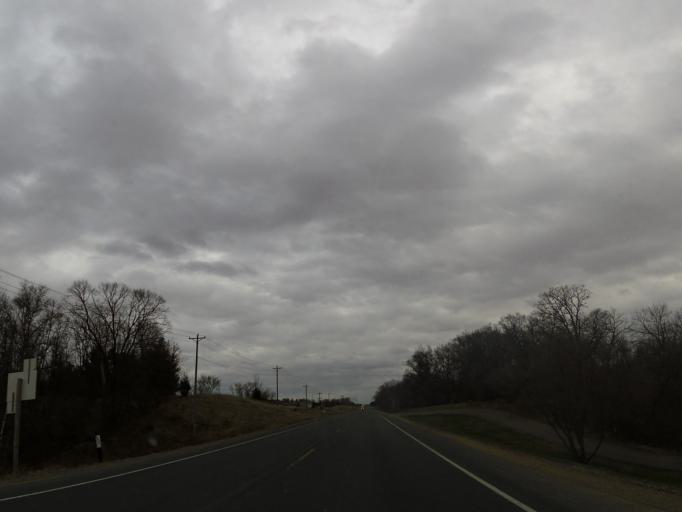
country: US
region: Wisconsin
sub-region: Saint Croix County
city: New Richmond
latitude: 45.1175
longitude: -92.5583
